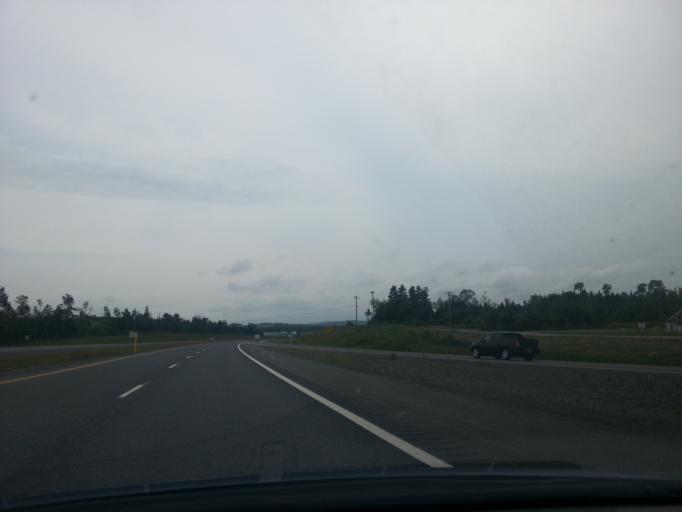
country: CA
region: New Brunswick
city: Florenceville-Bristol
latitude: 46.2842
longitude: -67.5786
